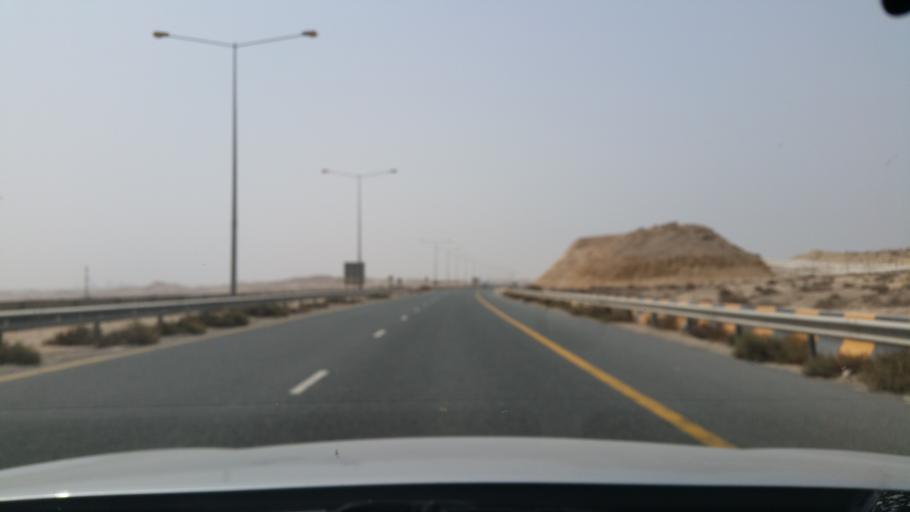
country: QA
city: Umm Bab
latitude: 25.2756
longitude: 50.7924
